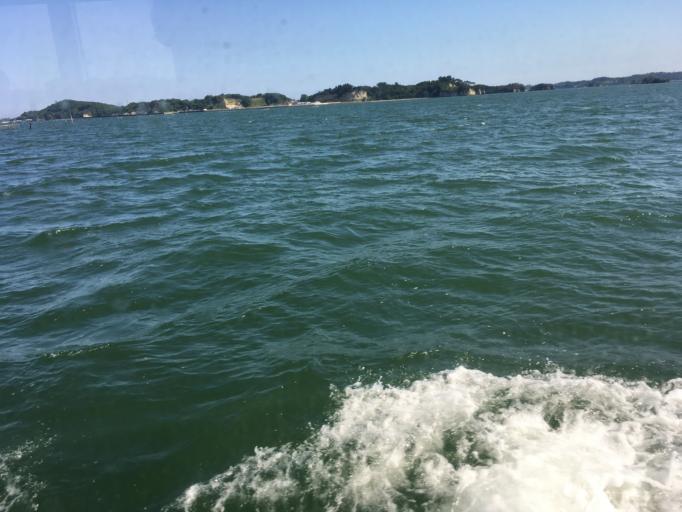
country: JP
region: Miyagi
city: Matsushima
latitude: 38.3491
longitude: 141.0840
